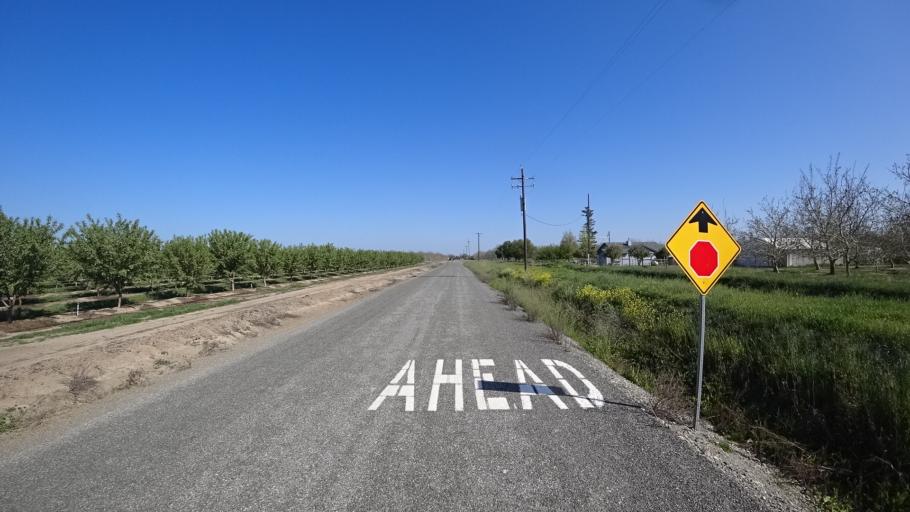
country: US
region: California
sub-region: Glenn County
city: Hamilton City
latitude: 39.6289
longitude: -122.0275
